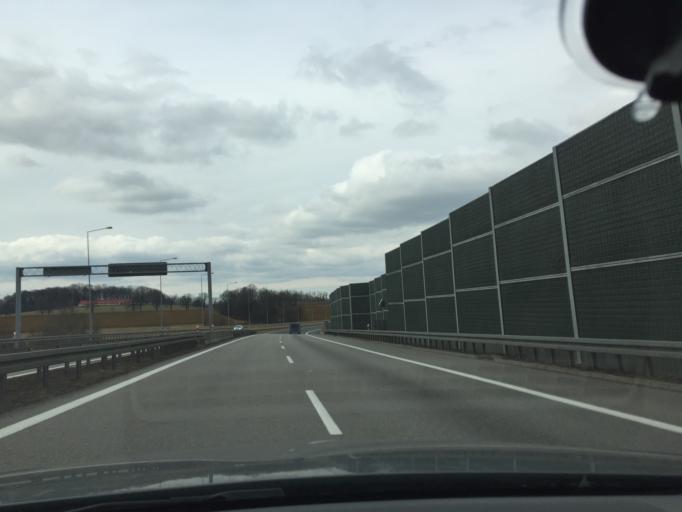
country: PL
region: Silesian Voivodeship
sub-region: Powiat bielski
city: Jasienica
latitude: 49.8051
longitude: 18.8865
